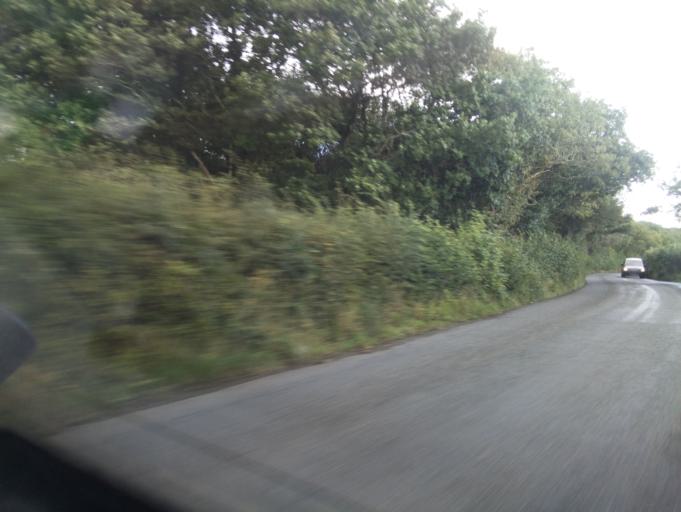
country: GB
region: England
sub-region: Devon
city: Ivybridge
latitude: 50.3792
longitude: -3.9148
